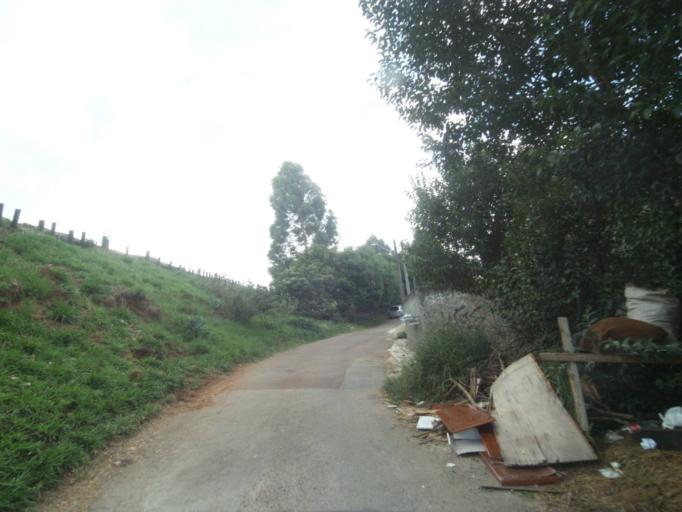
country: BR
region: Parana
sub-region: Pinhais
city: Pinhais
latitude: -25.4449
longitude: -49.2150
